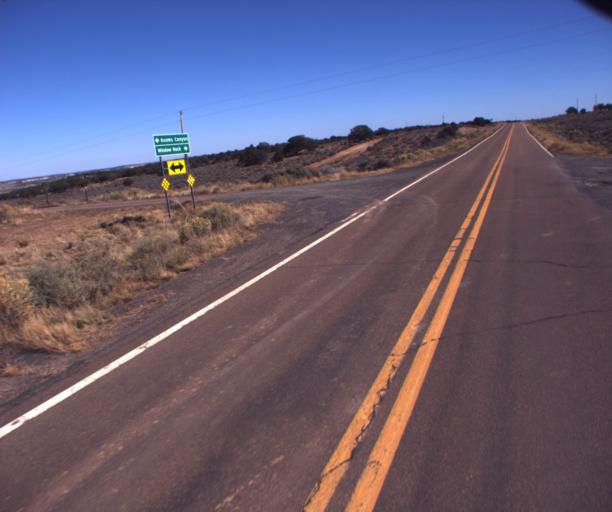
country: US
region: Arizona
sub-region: Apache County
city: Ganado
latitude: 35.7484
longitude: -109.9265
